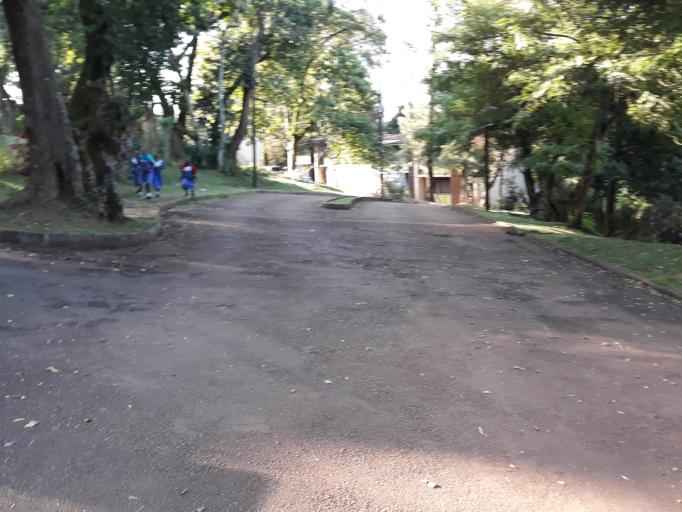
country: UG
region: Central Region
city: Kampala Central Division
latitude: 0.3377
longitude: 32.5659
